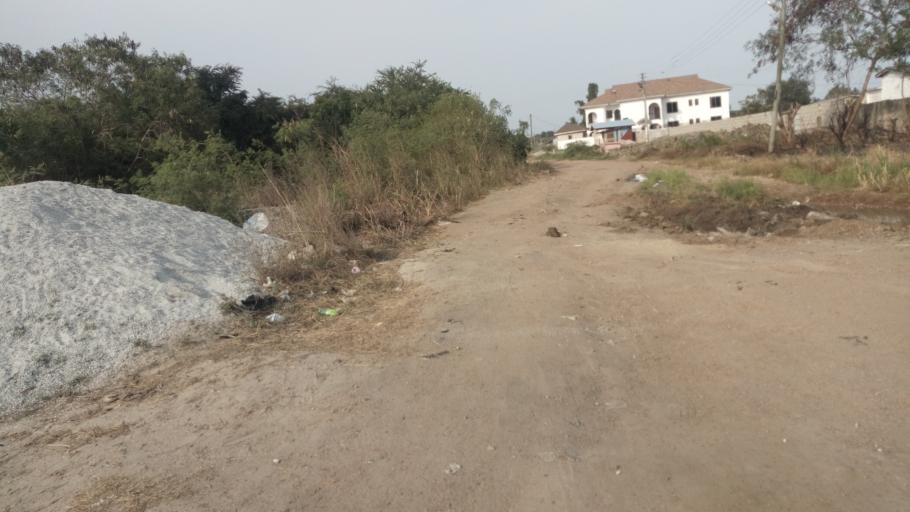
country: GH
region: Central
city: Winneba
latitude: 5.3499
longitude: -0.6343
